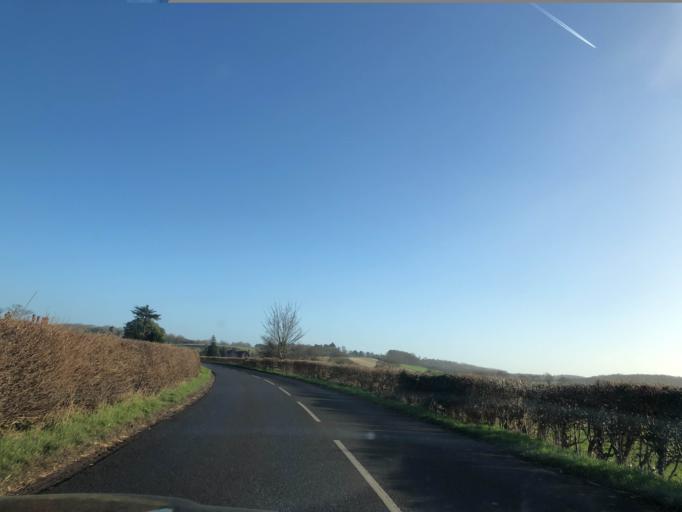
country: GB
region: England
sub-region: Warwickshire
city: Wellesbourne Mountford
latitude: 52.1919
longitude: -1.5804
